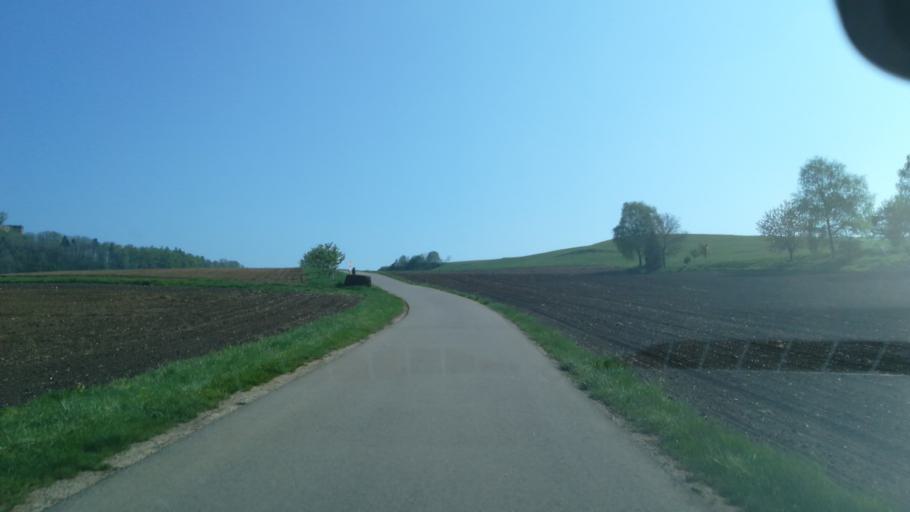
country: DE
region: Baden-Wuerttemberg
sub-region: Freiburg Region
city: Muhlhausen-Ehingen
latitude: 47.7989
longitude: 8.7944
